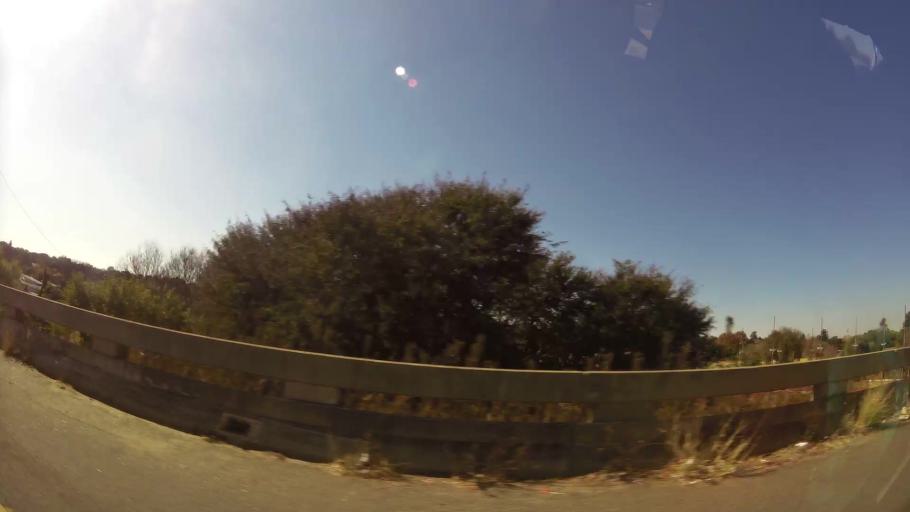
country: ZA
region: Gauteng
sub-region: City of Tshwane Metropolitan Municipality
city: Centurion
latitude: -25.8258
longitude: 28.2067
